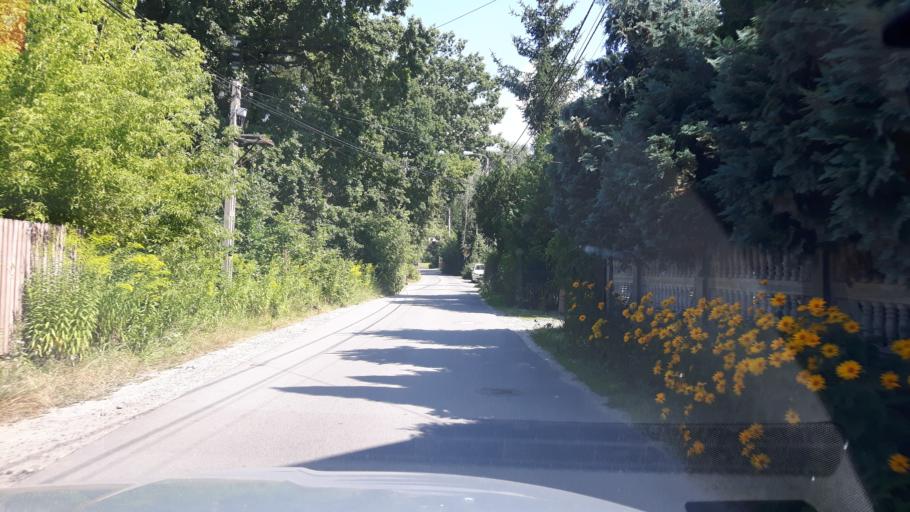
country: PL
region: Masovian Voivodeship
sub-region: Powiat minski
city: Sulejowek
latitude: 52.2311
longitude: 21.2689
